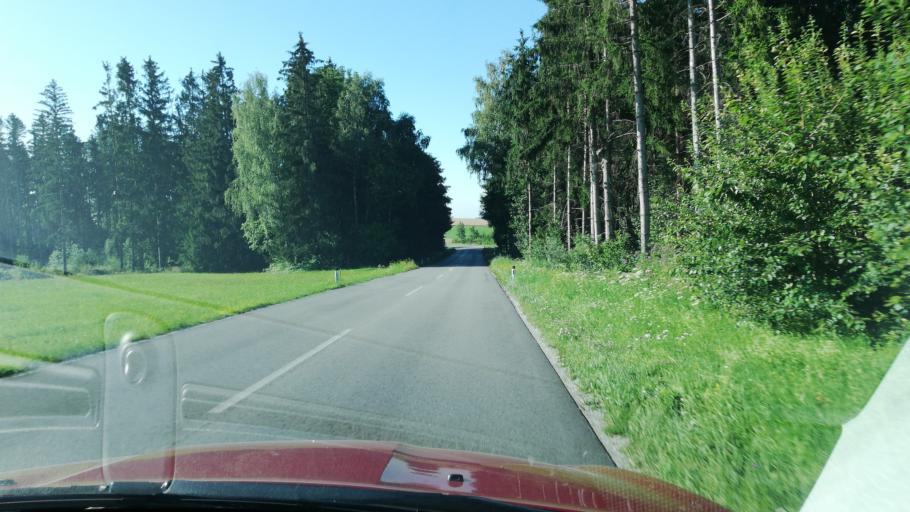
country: AT
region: Upper Austria
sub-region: Politischer Bezirk Rohrbach
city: Kleinzell im Muehlkreis
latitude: 48.4603
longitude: 14.0509
